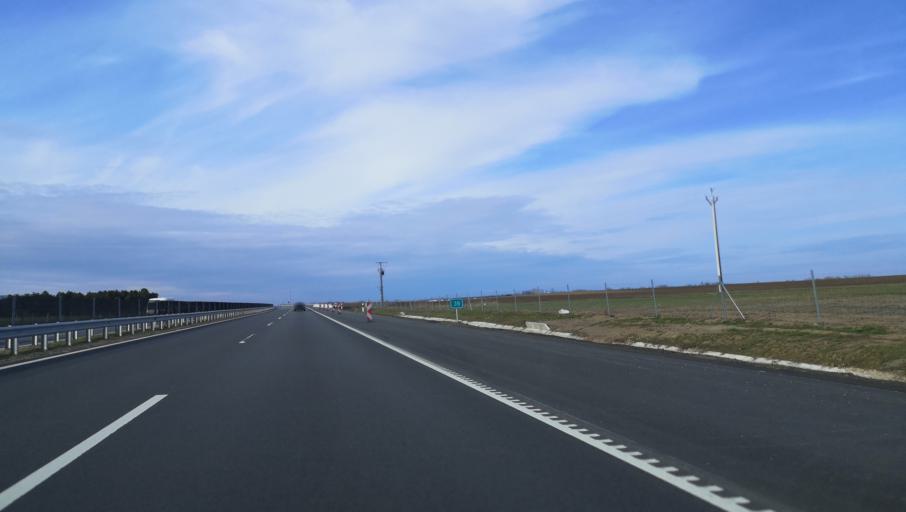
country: HU
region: Pest
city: Monor
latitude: 47.3723
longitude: 19.4744
